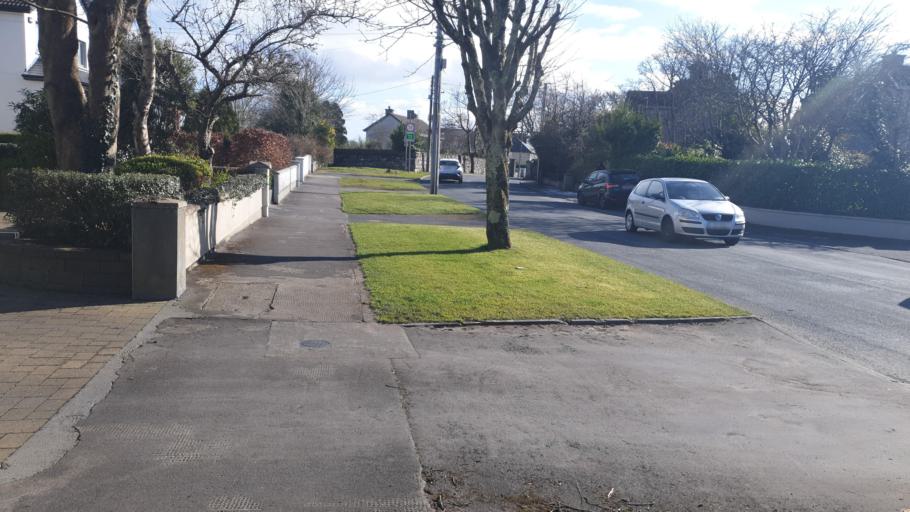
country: IE
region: Connaught
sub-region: County Galway
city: Gaillimh
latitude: 53.2712
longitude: -9.0719
